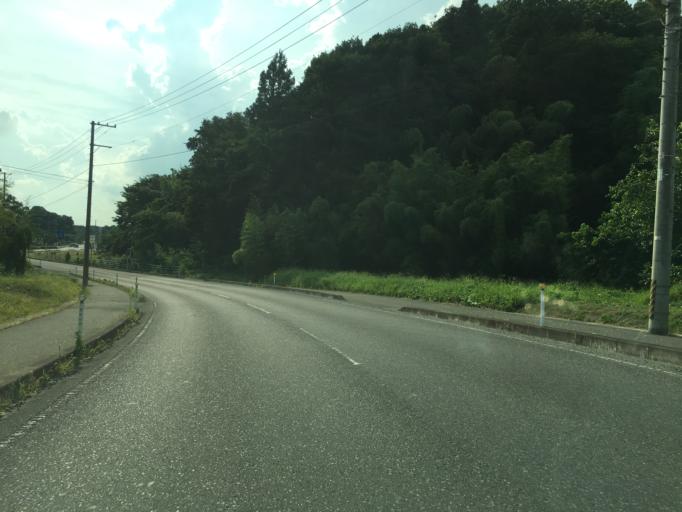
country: JP
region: Fukushima
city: Miharu
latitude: 37.4473
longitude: 140.4310
